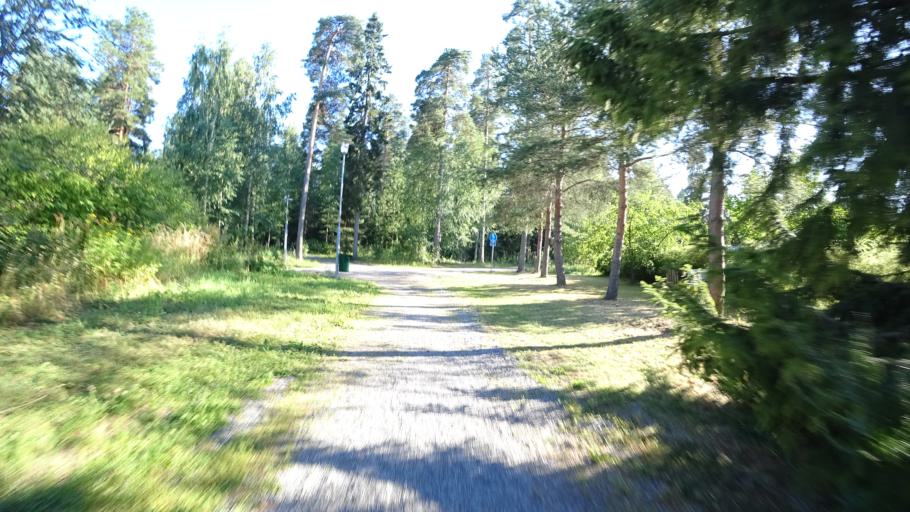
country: FI
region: Pirkanmaa
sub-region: Tampere
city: Pirkkala
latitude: 61.4980
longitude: 23.6147
